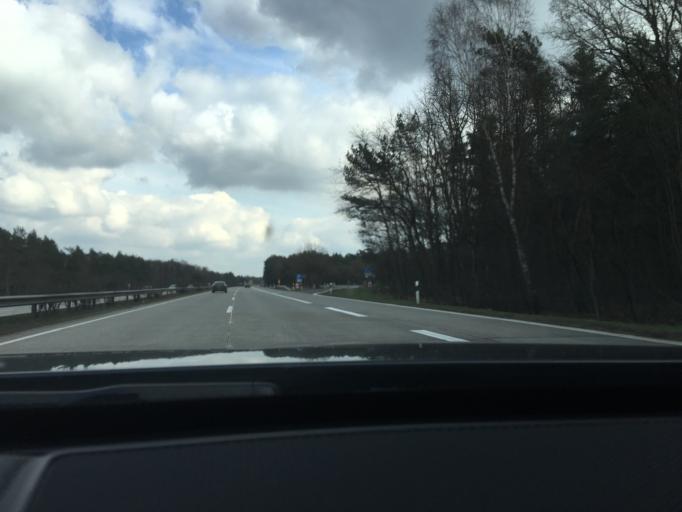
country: DE
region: Lower Saxony
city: Dotlingen
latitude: 52.9077
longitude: 8.3610
